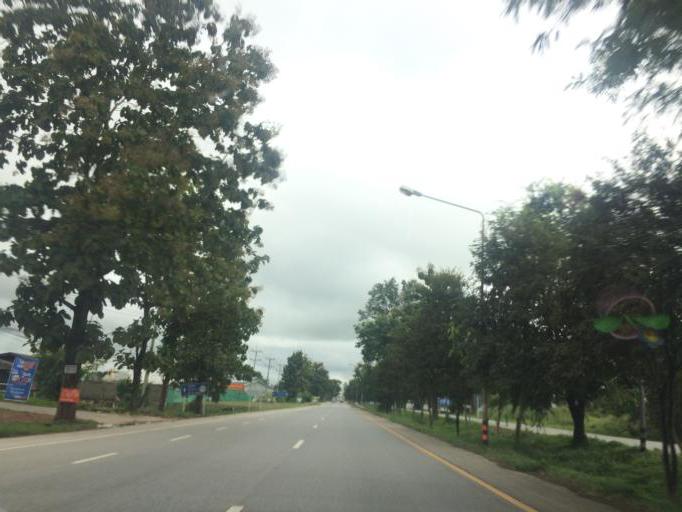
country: TH
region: Chiang Rai
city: Mae Lao
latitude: 19.8177
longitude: 99.7606
